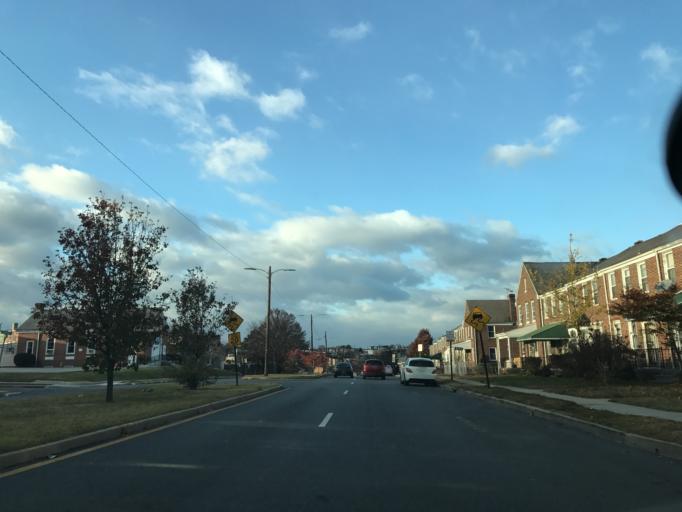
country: US
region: Maryland
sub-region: City of Baltimore
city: Baltimore
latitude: 39.3181
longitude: -76.5701
